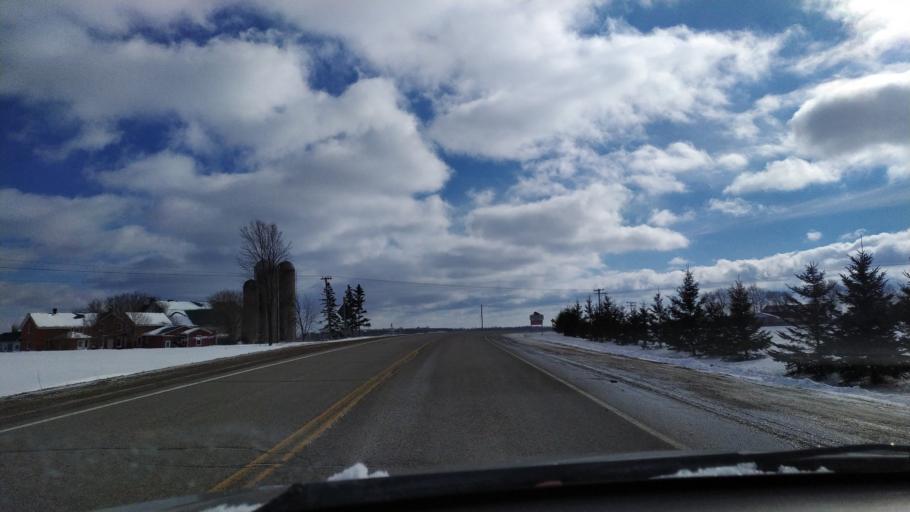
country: CA
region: Ontario
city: Waterloo
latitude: 43.5904
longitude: -80.6090
